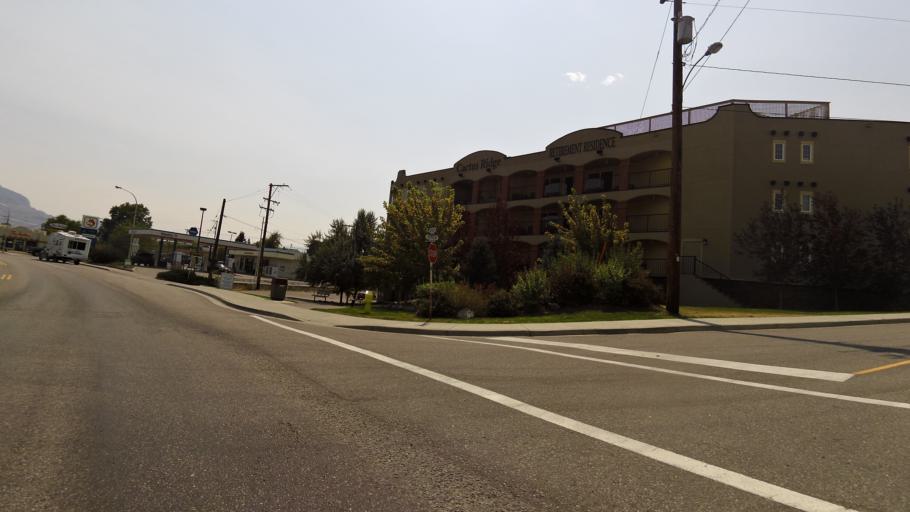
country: CA
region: British Columbia
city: Osoyoos
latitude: 49.0332
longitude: -119.4720
